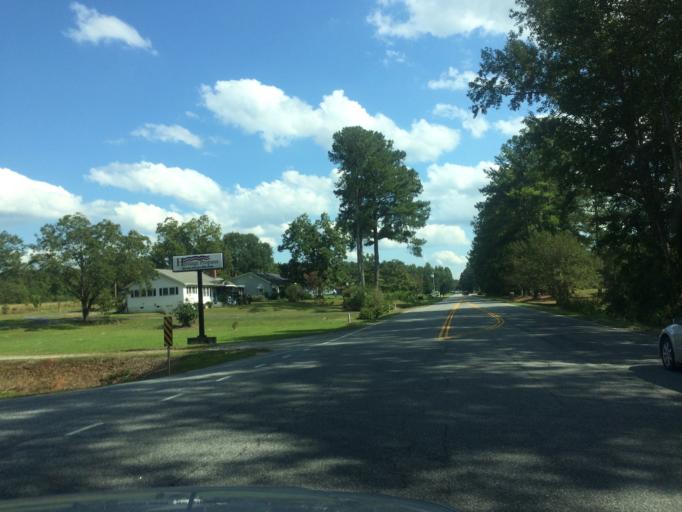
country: US
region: South Carolina
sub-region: Anderson County
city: Honea Path
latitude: 34.4675
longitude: -82.4237
